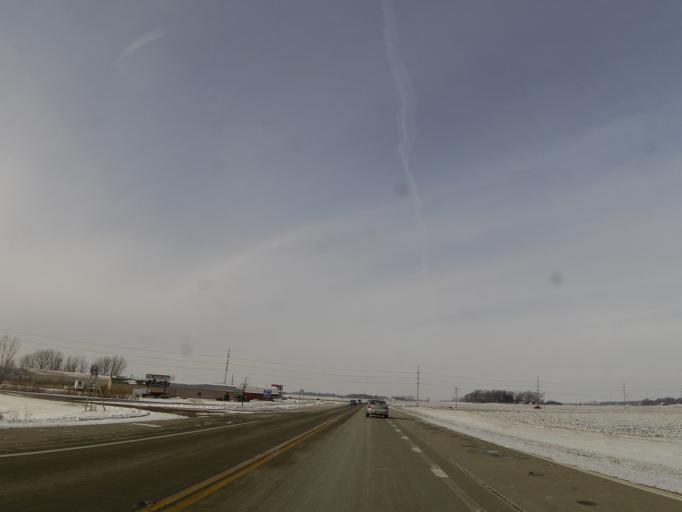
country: US
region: Minnesota
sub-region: McLeod County
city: Hutchinson
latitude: 44.8939
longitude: -94.3205
